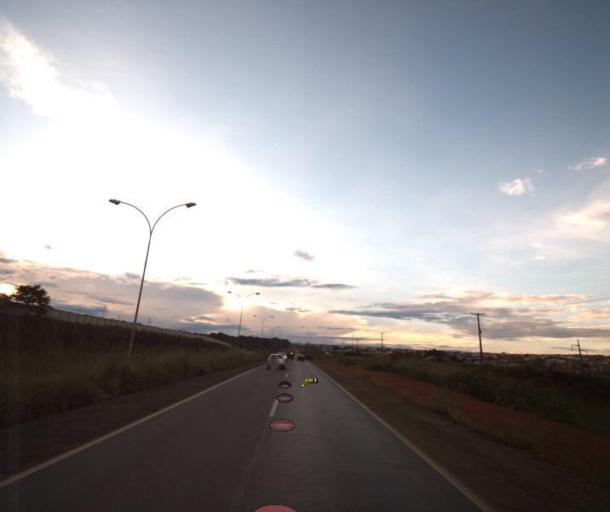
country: BR
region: Goias
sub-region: Anapolis
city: Anapolis
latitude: -16.2966
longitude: -48.9301
